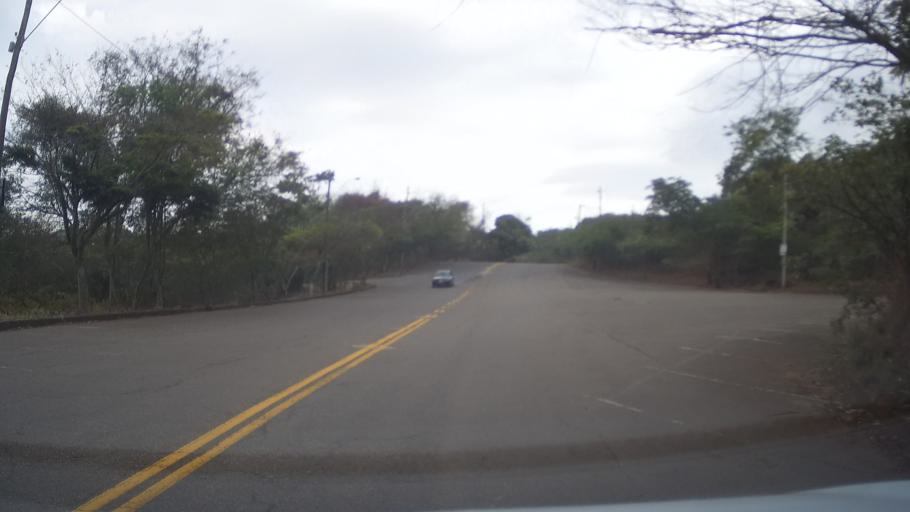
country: BR
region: Minas Gerais
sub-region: Belo Horizonte
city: Belo Horizonte
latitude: -19.9531
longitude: -43.9070
